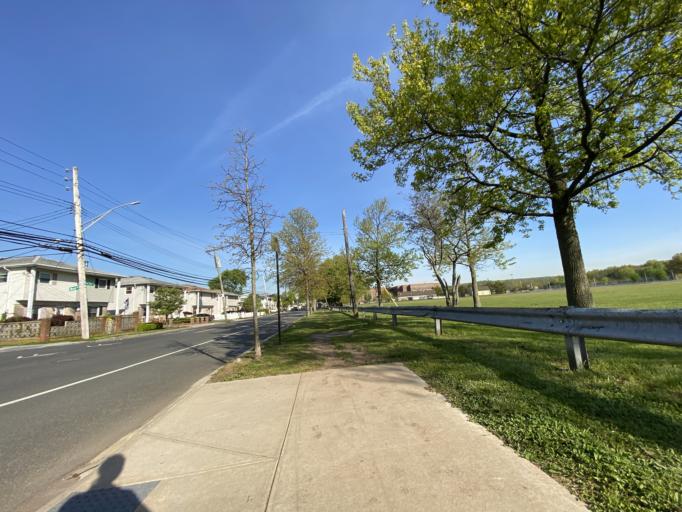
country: US
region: New York
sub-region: Richmond County
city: Staten Island
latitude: 40.5675
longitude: -74.1037
